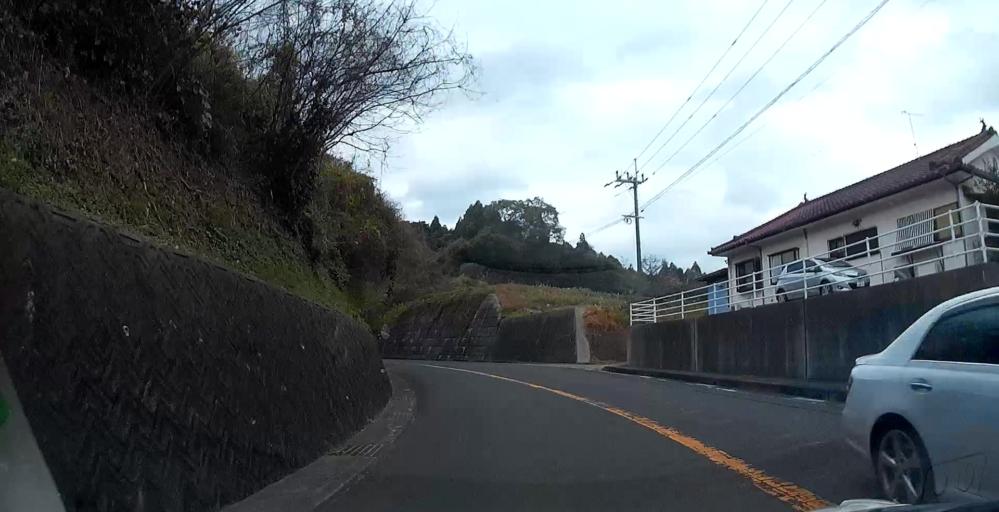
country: JP
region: Kagoshima
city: Akune
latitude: 32.1027
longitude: 130.1667
